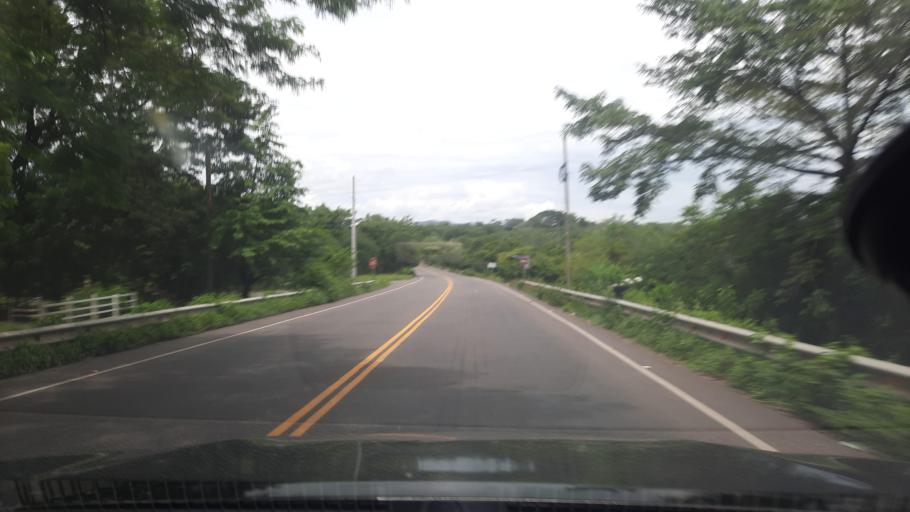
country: HN
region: Valle
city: Nacaome
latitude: 13.5352
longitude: -87.4633
